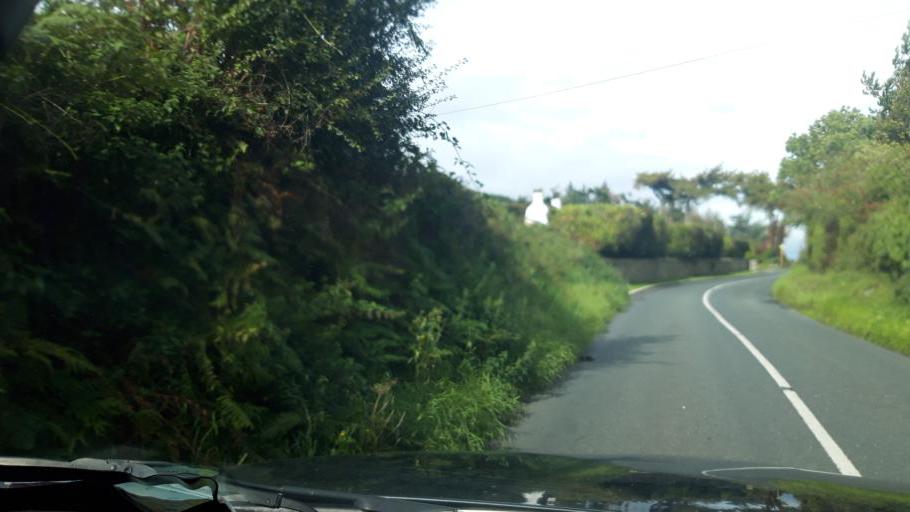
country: IE
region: Leinster
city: Sandyford
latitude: 53.2367
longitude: -6.2219
